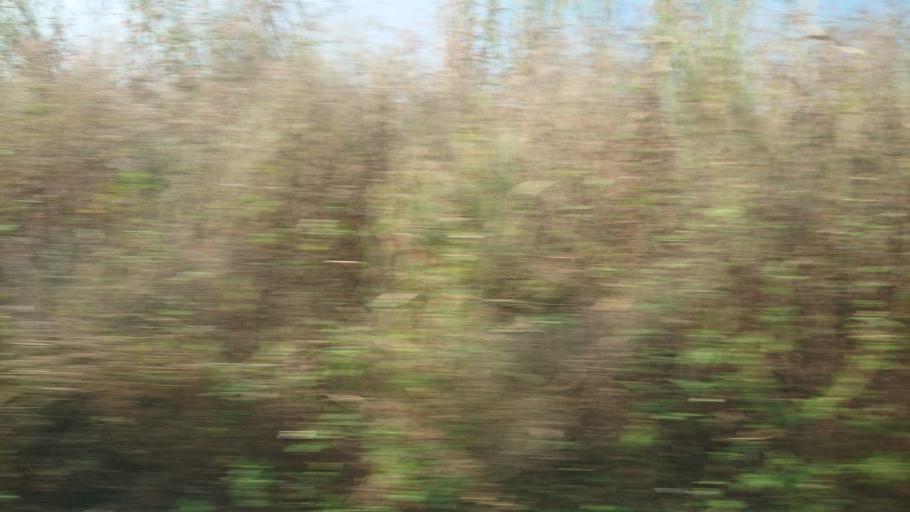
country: TW
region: Taiwan
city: Lugu
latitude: 23.7349
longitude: 120.6588
